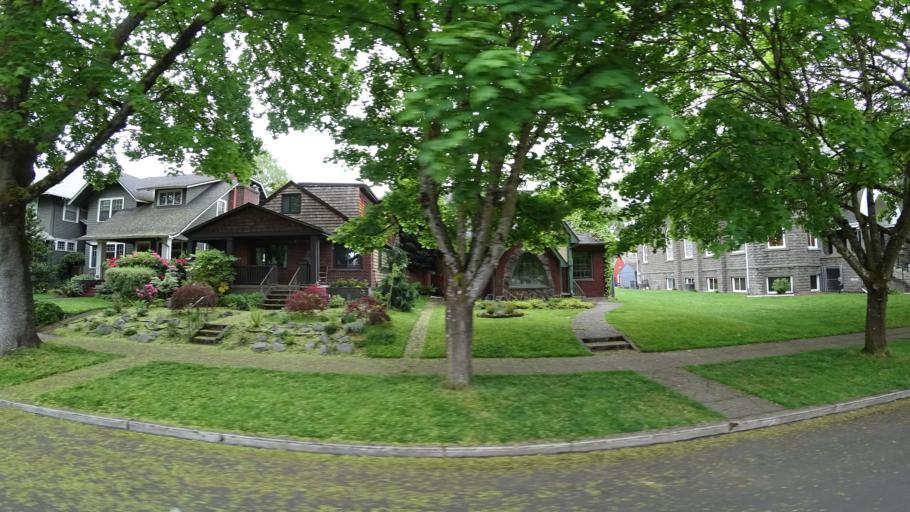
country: US
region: Oregon
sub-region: Multnomah County
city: Portland
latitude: 45.5102
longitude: -122.6492
